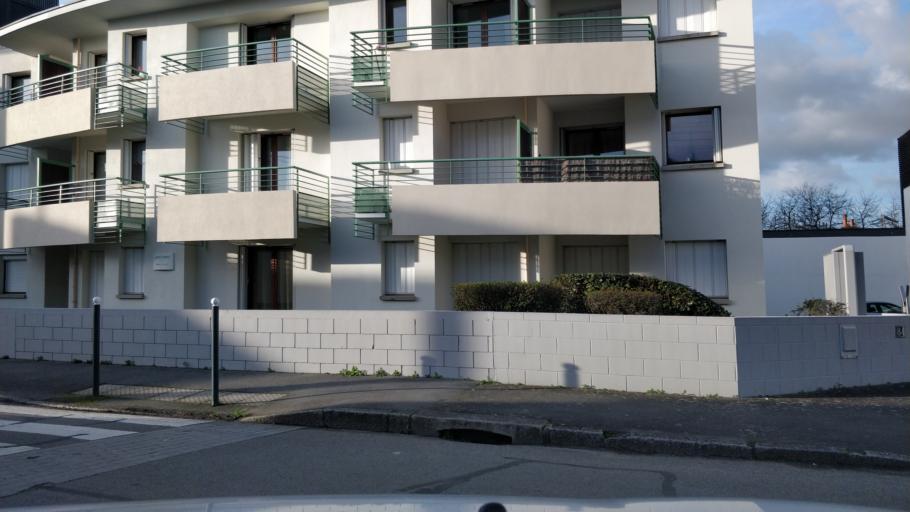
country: FR
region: Brittany
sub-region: Departement d'Ille-et-Vilaine
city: Rennes
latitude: 48.1047
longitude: -1.7050
